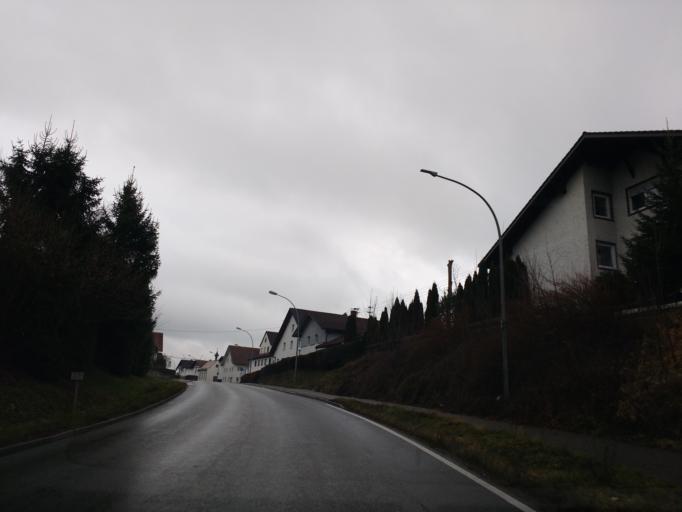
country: DE
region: Bavaria
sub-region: Swabia
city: Neuburg
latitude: 47.7674
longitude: 10.3361
